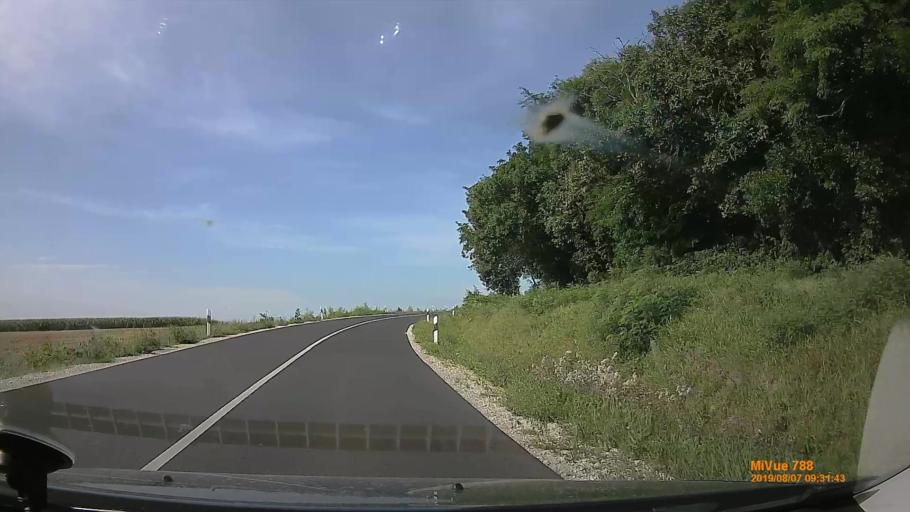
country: HU
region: Zala
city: Sarmellek
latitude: 46.7400
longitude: 17.1706
